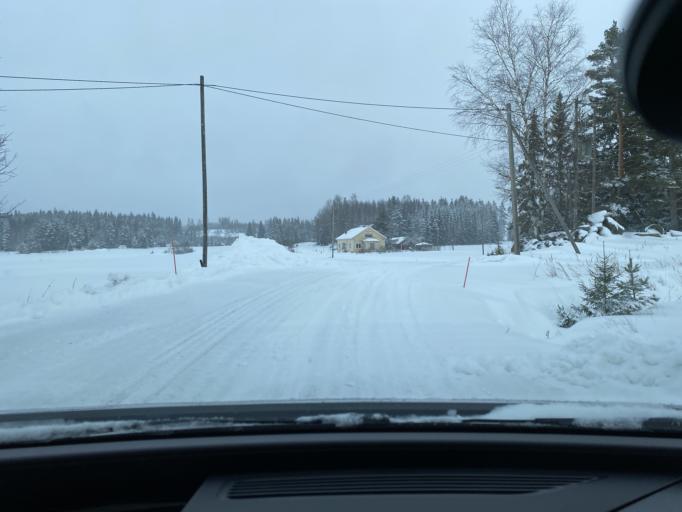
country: FI
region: Haeme
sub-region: Forssa
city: Humppila
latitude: 61.0128
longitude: 23.3043
